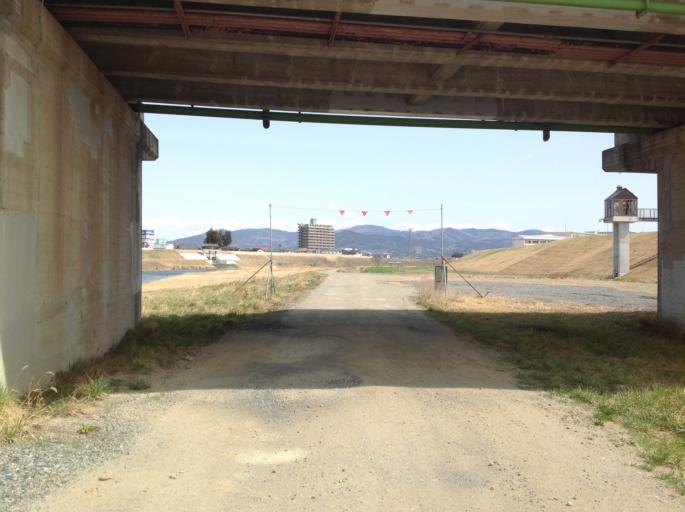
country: JP
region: Iwate
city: Ichinoseki
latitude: 38.9327
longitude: 141.1319
